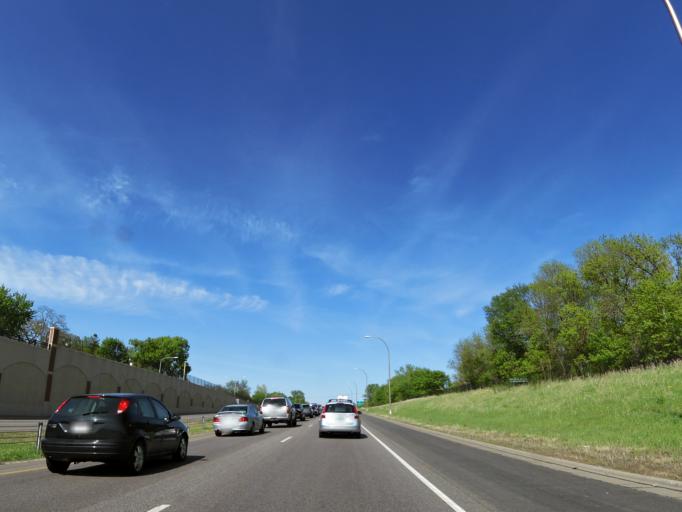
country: US
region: Minnesota
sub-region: Ramsey County
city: North Saint Paul
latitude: 45.0160
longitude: -92.9913
